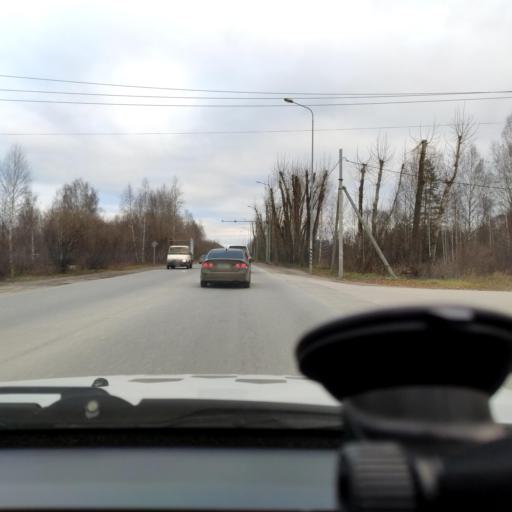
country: RU
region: Perm
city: Perm
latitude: 58.0923
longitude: 56.3145
